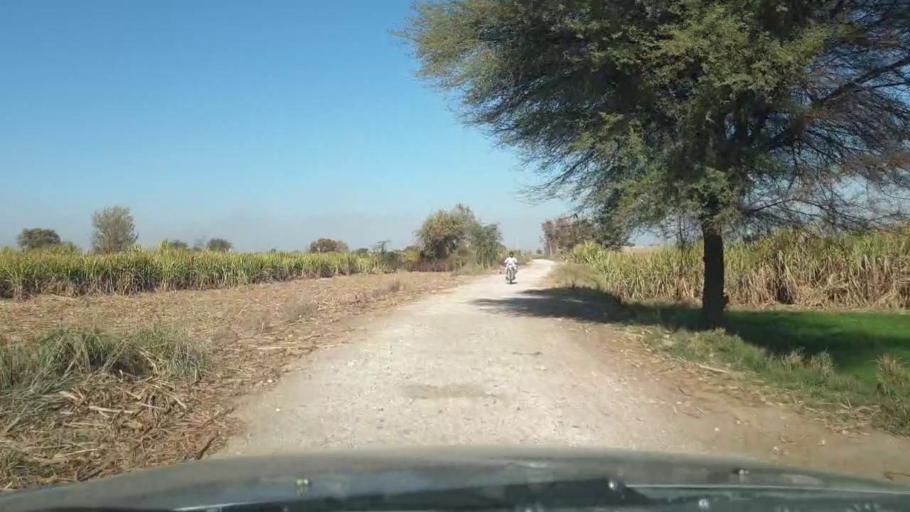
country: PK
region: Sindh
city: Ghotki
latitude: 28.0499
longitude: 69.2406
